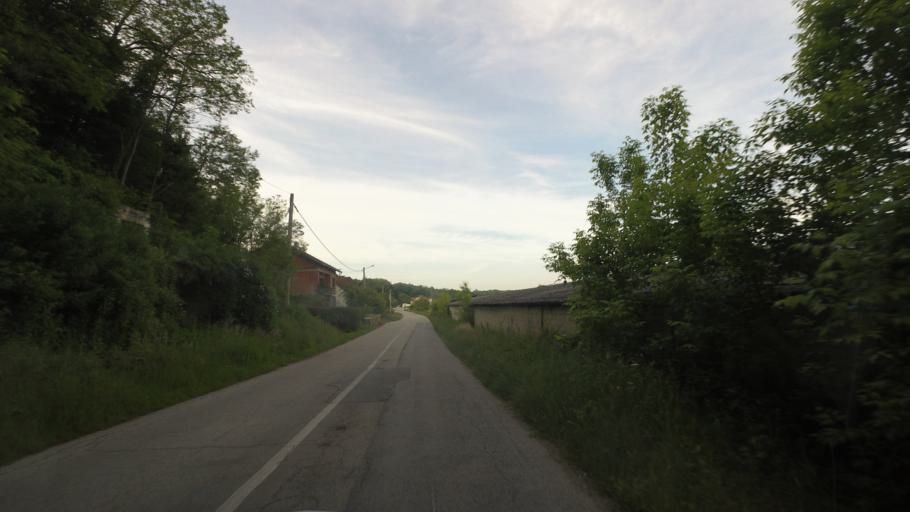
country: HR
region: Sisacko-Moslavacka
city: Gvozd
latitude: 45.2981
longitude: 15.9765
